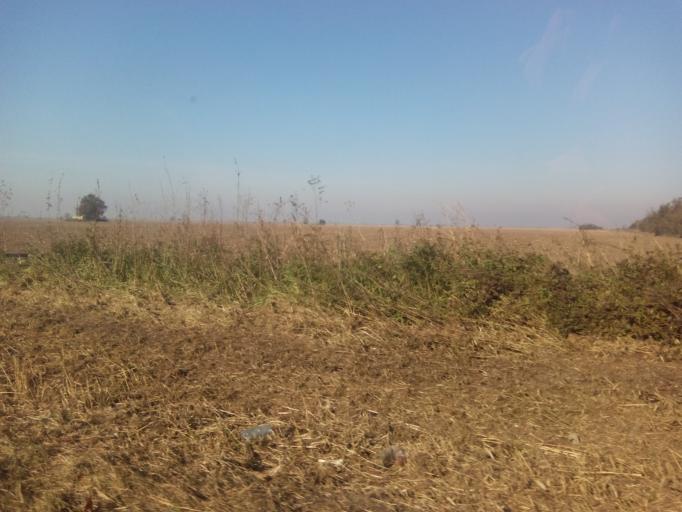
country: RS
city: Celarevo
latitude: 45.2559
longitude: 19.4927
